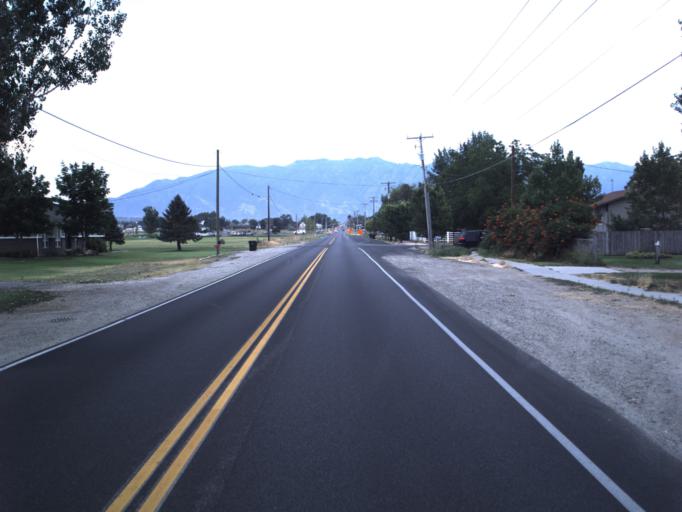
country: US
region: Utah
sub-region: Davis County
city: Syracuse
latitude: 41.0892
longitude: -112.0926
